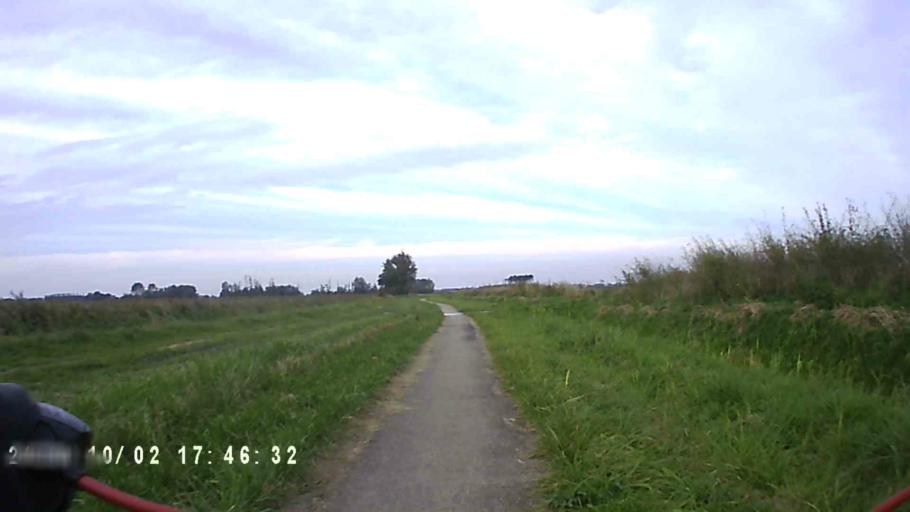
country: NL
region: Groningen
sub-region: Gemeente Zuidhorn
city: Oldehove
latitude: 53.3348
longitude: 6.3957
